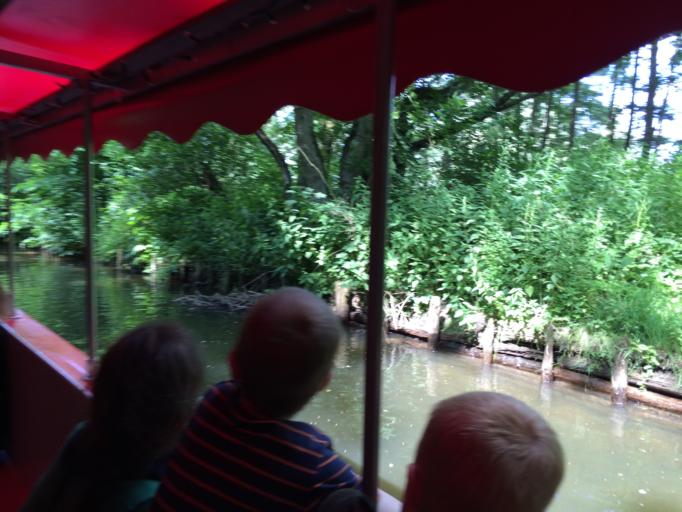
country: DK
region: South Denmark
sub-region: Odense Kommune
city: Odense
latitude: 55.3754
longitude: 10.3737
